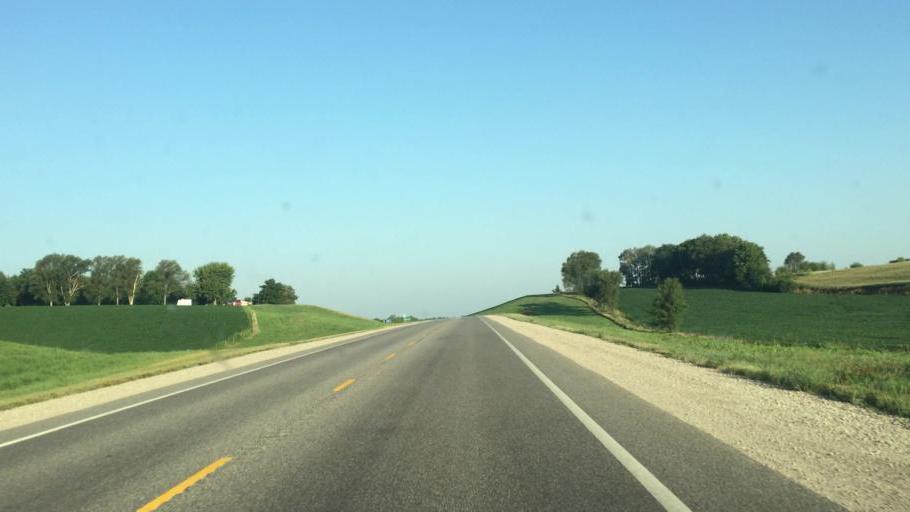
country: US
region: Kansas
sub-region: Doniphan County
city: Troy
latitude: 39.7936
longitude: -95.0790
